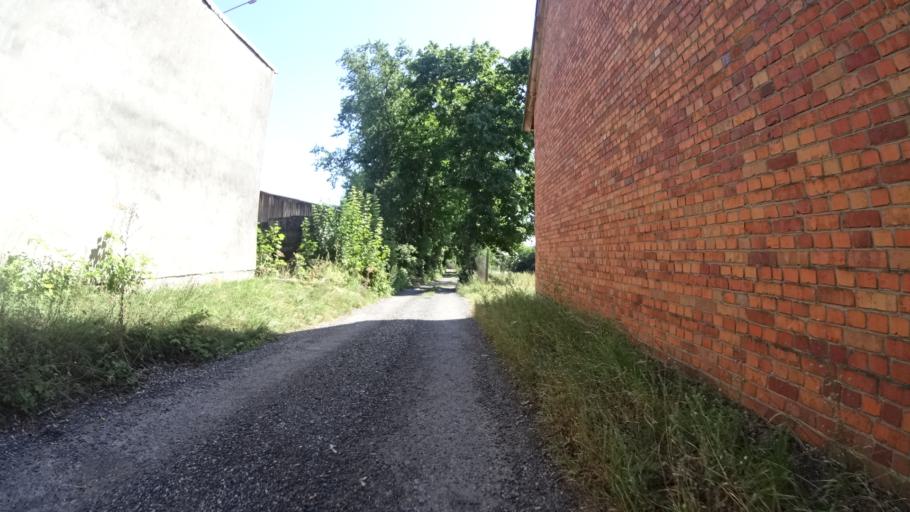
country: PL
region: Masovian Voivodeship
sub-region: Powiat bialobrzeski
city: Bialobrzegi
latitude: 51.6703
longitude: 20.9205
